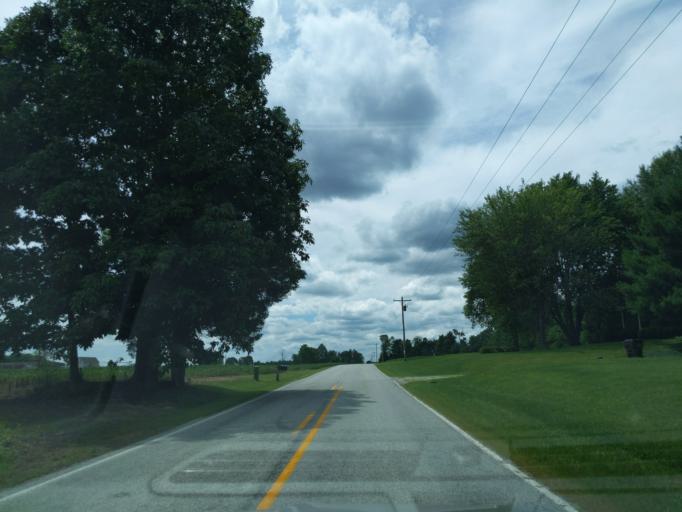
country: US
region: Indiana
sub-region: Ripley County
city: Batesville
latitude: 39.2389
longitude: -85.2596
